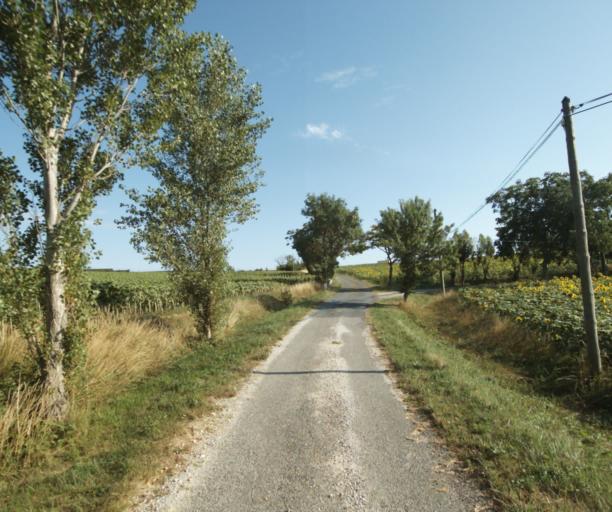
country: FR
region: Midi-Pyrenees
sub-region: Departement de la Haute-Garonne
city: Saint-Felix-Lauragais
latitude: 43.4422
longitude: 1.8127
